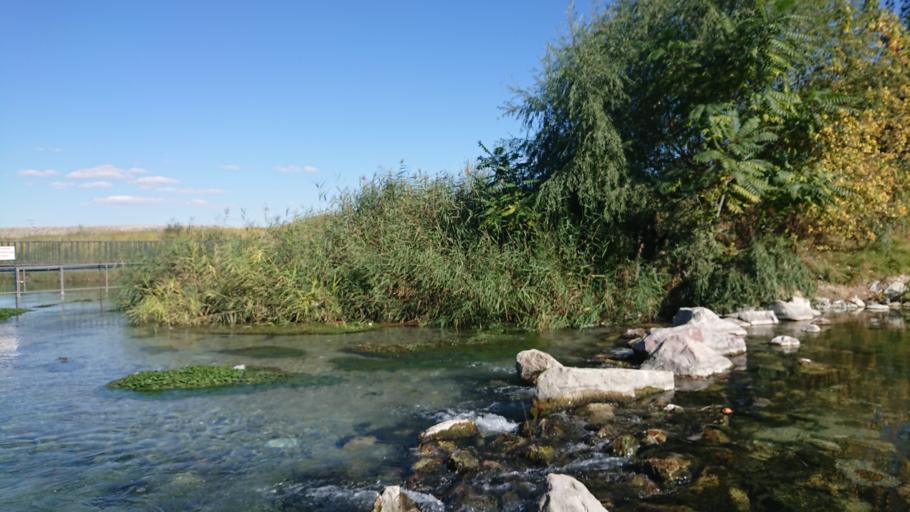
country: TR
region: Eskisehir
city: Cifteler
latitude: 39.3535
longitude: 31.0589
